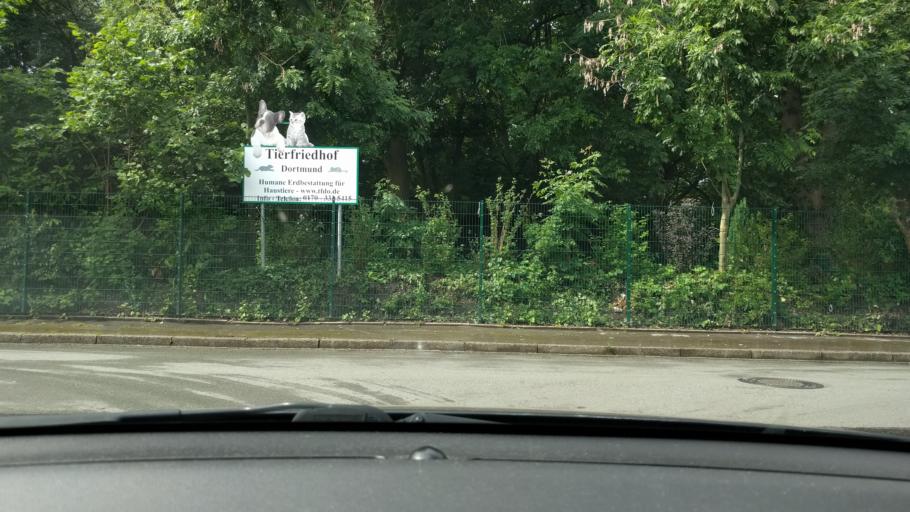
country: DE
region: North Rhine-Westphalia
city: Witten
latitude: 51.4899
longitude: 7.3694
